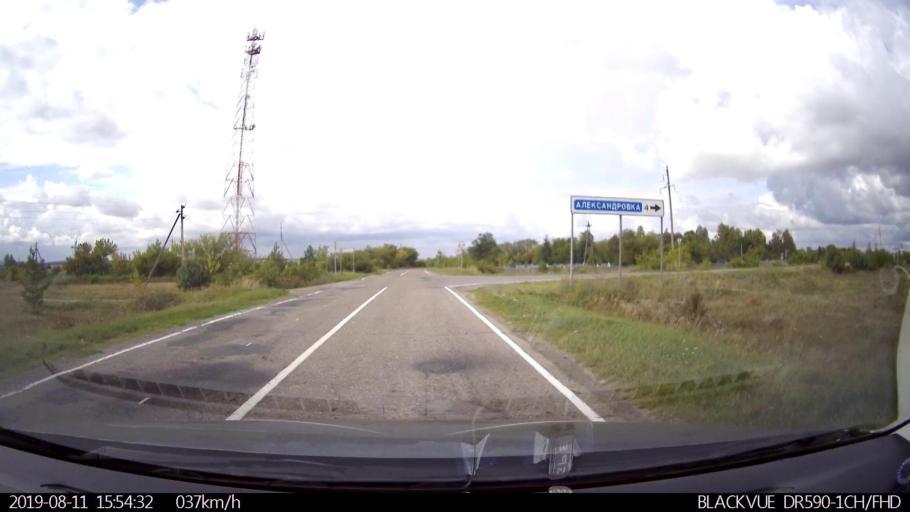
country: RU
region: Ulyanovsk
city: Ignatovka
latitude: 53.9417
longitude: 47.6563
